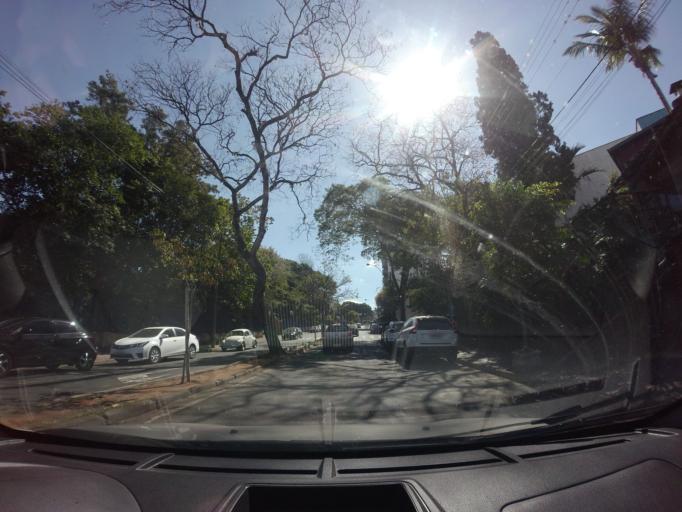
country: BR
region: Sao Paulo
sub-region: Piracicaba
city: Piracicaba
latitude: -22.7146
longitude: -47.6475
